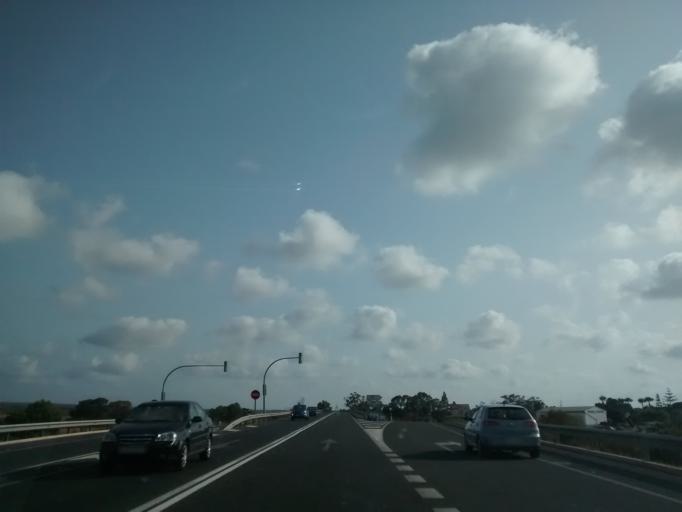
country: ES
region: Valencia
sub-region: Provincia de Alicante
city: Santa Pola
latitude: 38.2619
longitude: -0.5443
